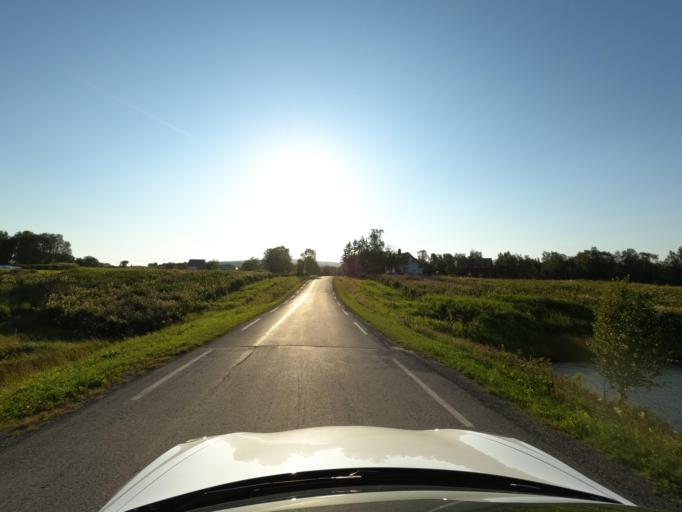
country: NO
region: Troms
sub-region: Skanland
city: Evenskjer
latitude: 68.4639
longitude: 16.6641
